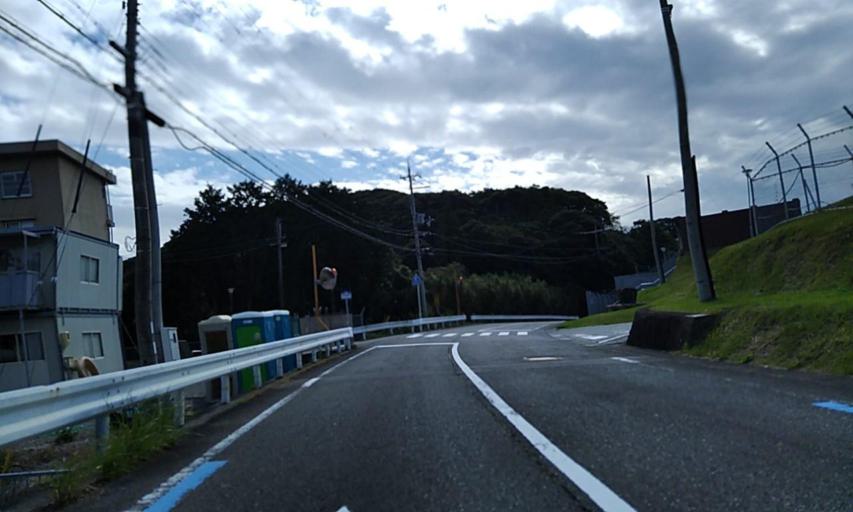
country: JP
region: Wakayama
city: Shingu
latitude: 33.4671
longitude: 135.8303
